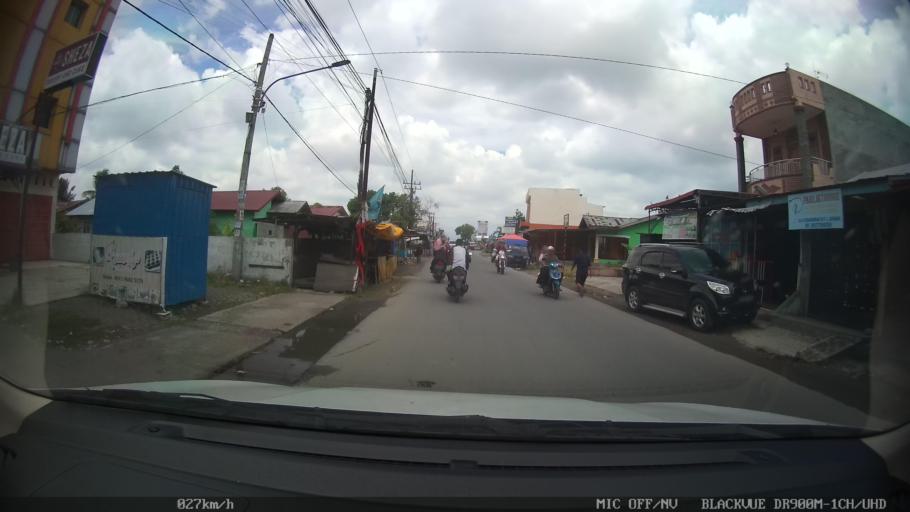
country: ID
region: North Sumatra
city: Medan
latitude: 3.6204
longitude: 98.7352
